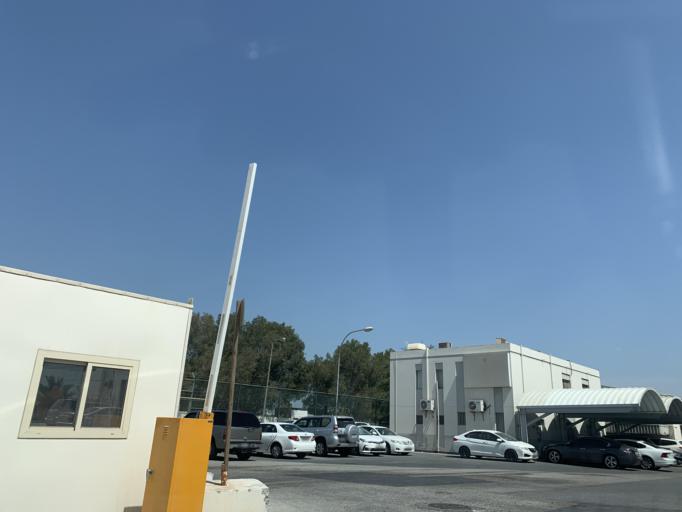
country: BH
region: Muharraq
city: Al Muharraq
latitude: 26.2693
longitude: 50.6207
